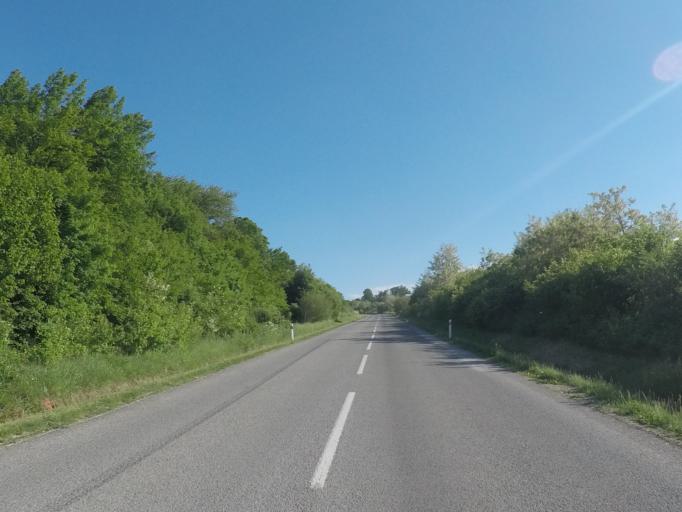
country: SK
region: Kosicky
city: Roznava
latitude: 48.5409
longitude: 20.4081
